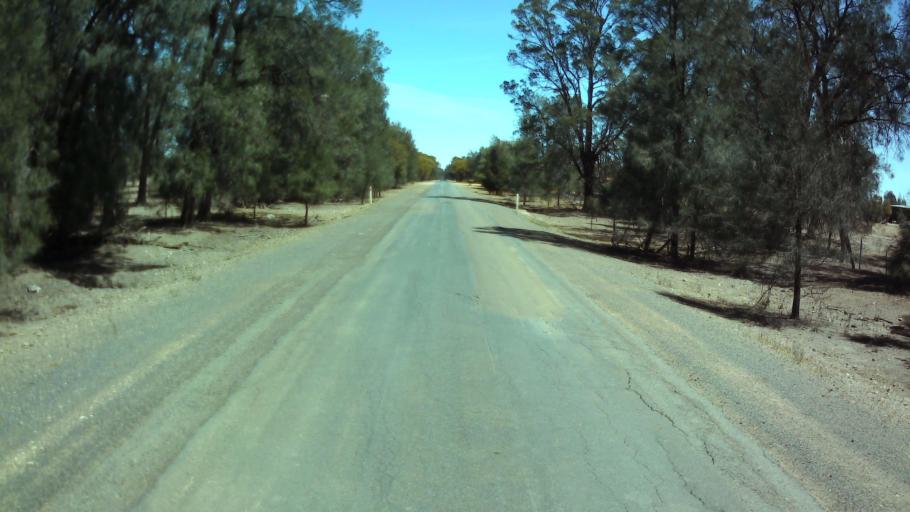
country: AU
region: New South Wales
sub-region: Weddin
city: Grenfell
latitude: -33.8689
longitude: 147.6923
